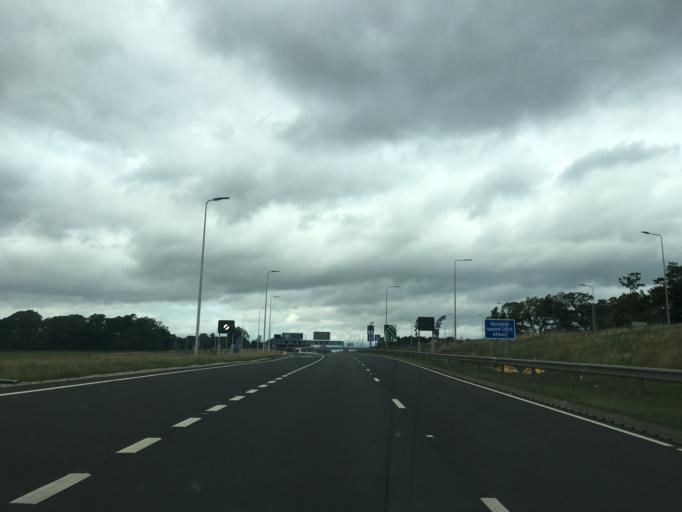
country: GB
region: Scotland
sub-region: Edinburgh
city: Queensferry
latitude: 55.9782
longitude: -3.3851
